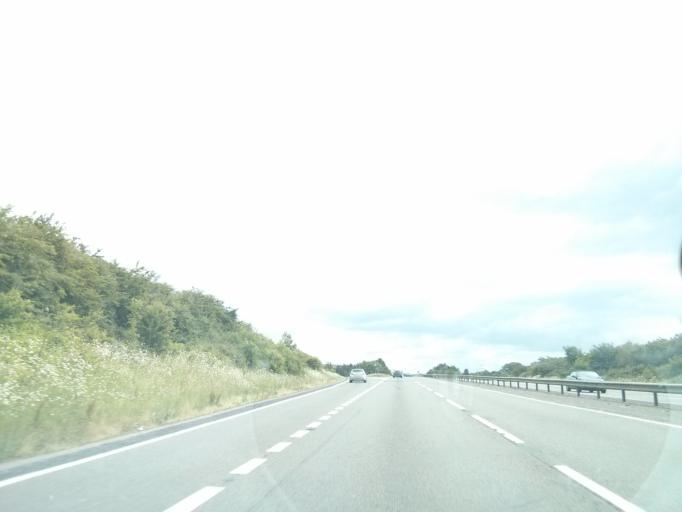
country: GB
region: England
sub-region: Northamptonshire
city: Thrapston
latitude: 52.3898
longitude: -0.5287
